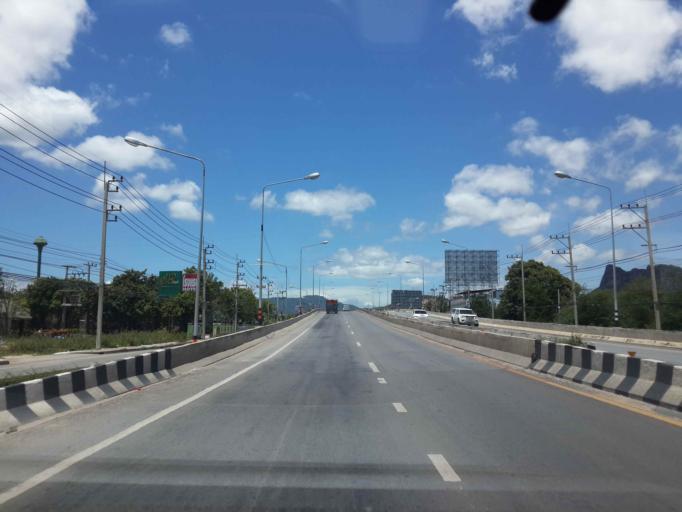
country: TH
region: Phetchaburi
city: Cha-am
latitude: 12.8043
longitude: 99.9695
